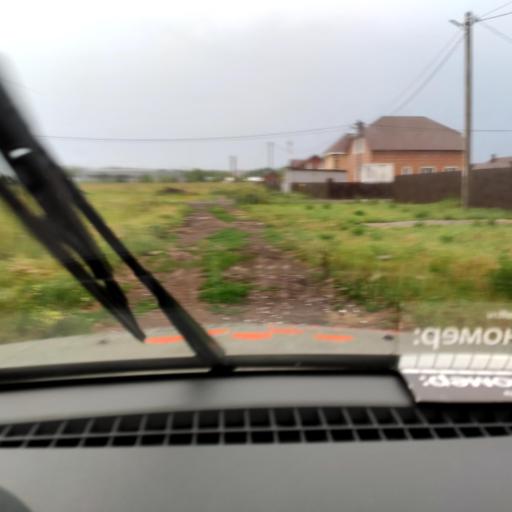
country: RU
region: Bashkortostan
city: Mikhaylovka
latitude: 54.8628
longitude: 55.7410
